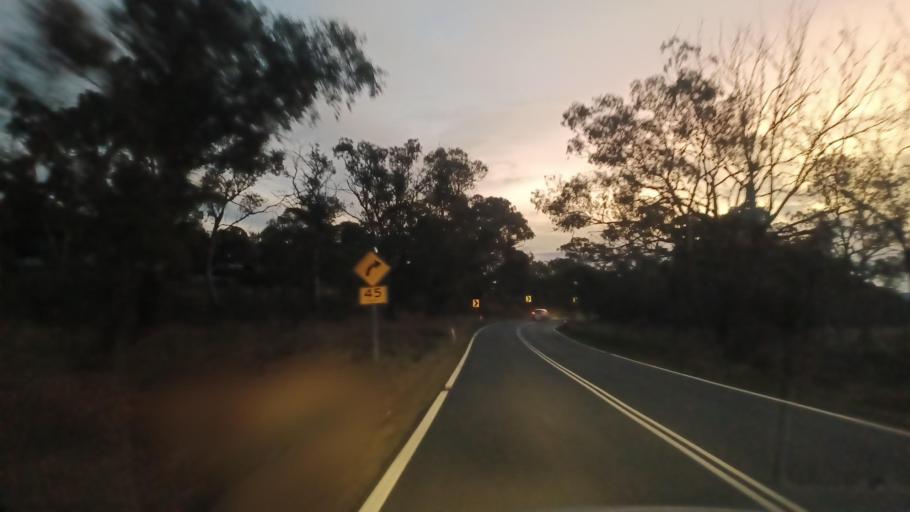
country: AU
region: Australian Capital Territory
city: Belconnen
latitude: -35.1890
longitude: 149.0564
